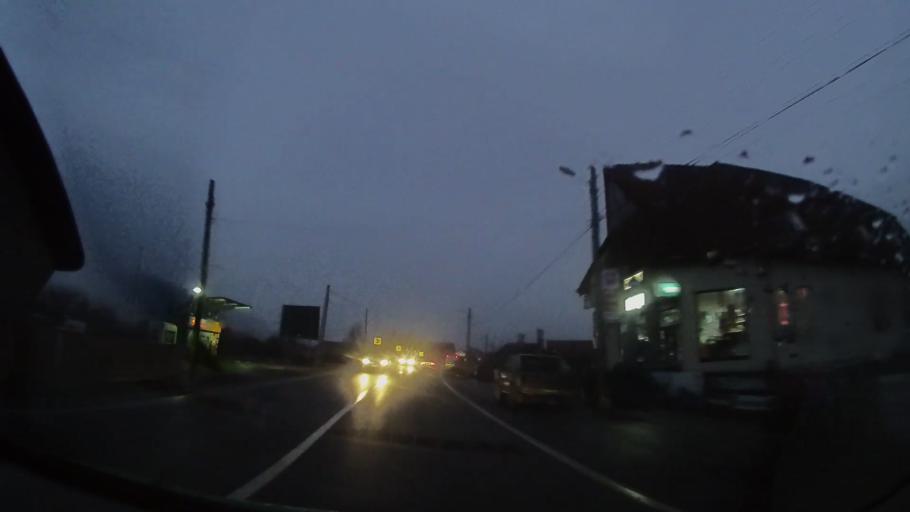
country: RO
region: Harghita
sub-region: Comuna Ditrau
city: Ditrau
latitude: 46.8068
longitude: 25.4932
